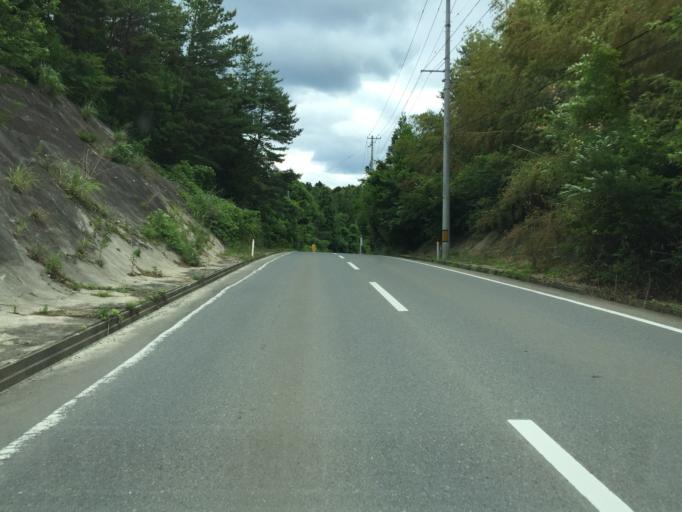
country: JP
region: Fukushima
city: Namie
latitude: 37.6505
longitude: 141.0142
